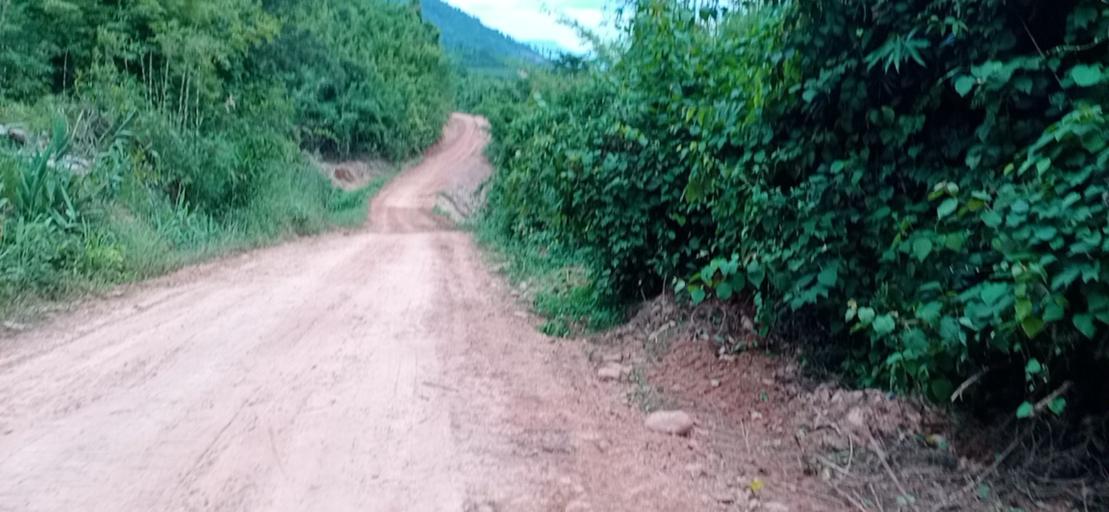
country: TH
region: Changwat Bueng Kan
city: Pak Khat
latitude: 18.5533
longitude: 103.1691
